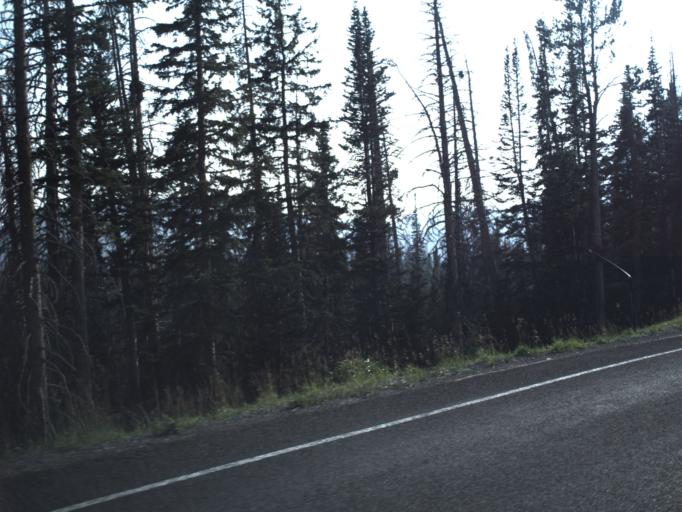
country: US
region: Utah
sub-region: Summit County
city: Kamas
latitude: 40.7124
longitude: -110.8775
